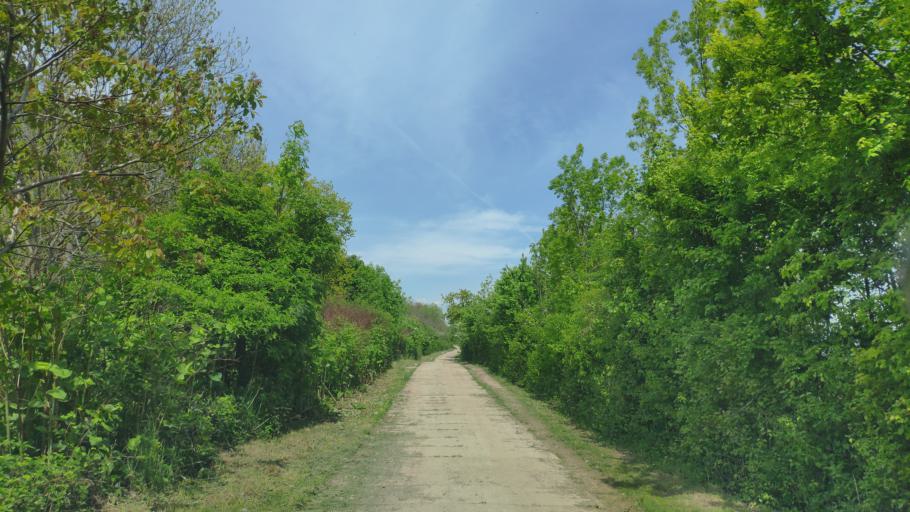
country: SK
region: Kosicky
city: Secovce
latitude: 48.6855
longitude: 21.6080
